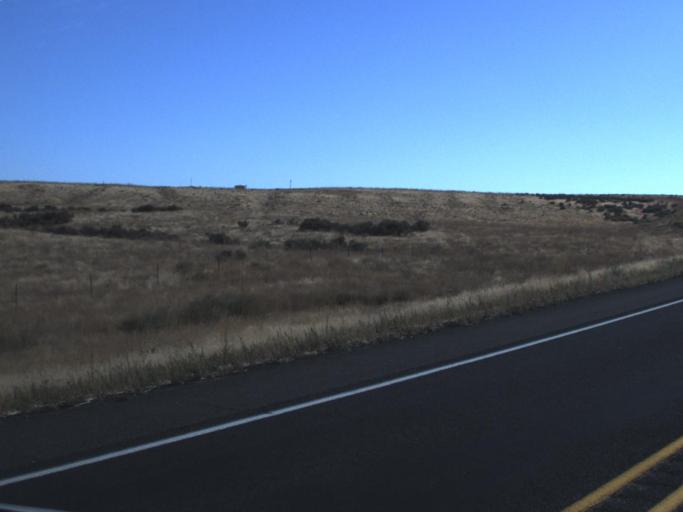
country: US
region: Washington
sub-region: Franklin County
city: Basin City
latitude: 46.5697
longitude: -119.0012
